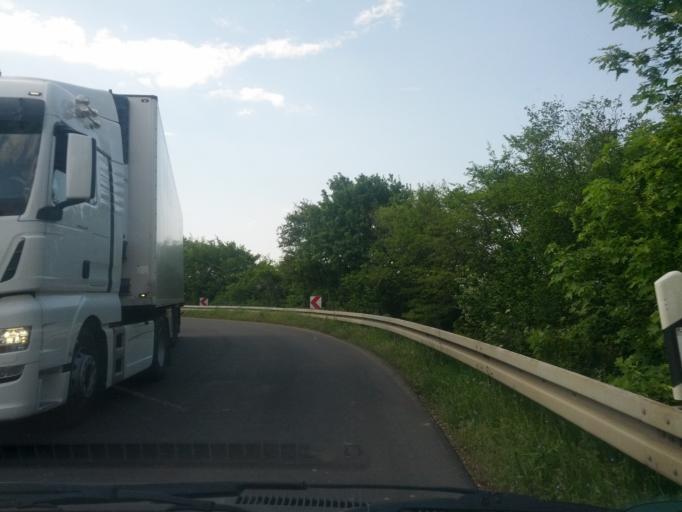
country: DE
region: Baden-Wuerttemberg
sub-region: Freiburg Region
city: Ettenheim
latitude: 48.2641
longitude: 7.8004
